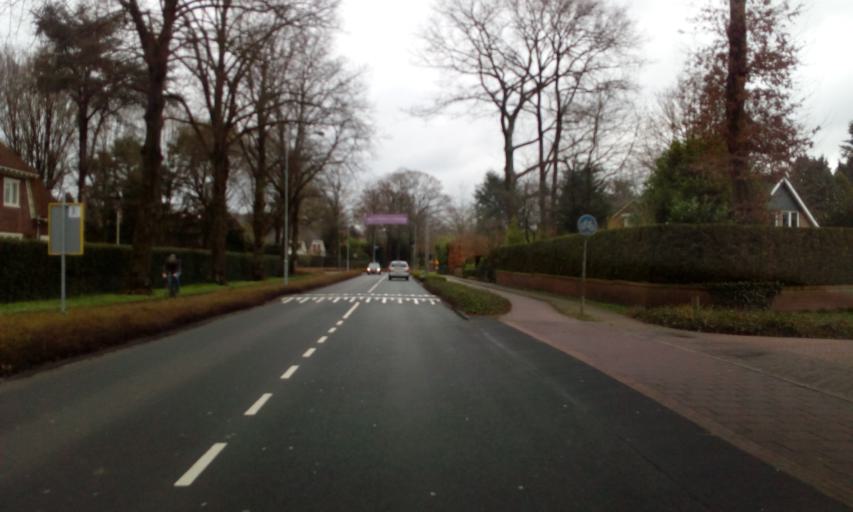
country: NL
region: North Holland
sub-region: Gemeente Laren
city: Laren
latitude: 52.2533
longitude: 5.2164
